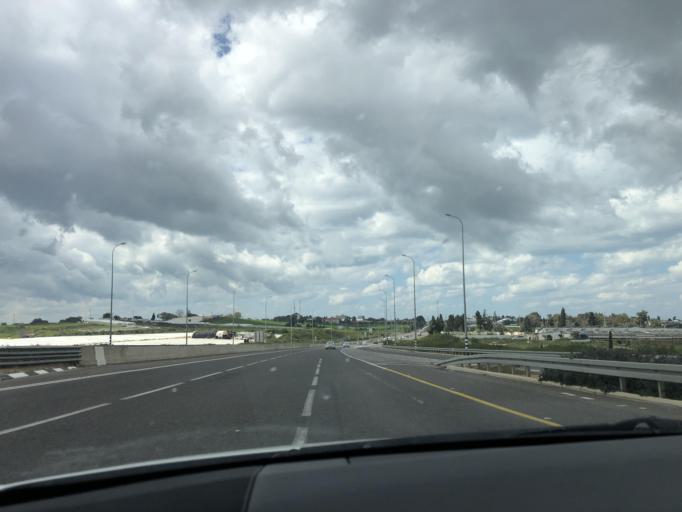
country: IL
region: Central District
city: Even Yehuda
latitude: 32.2552
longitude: 34.8881
